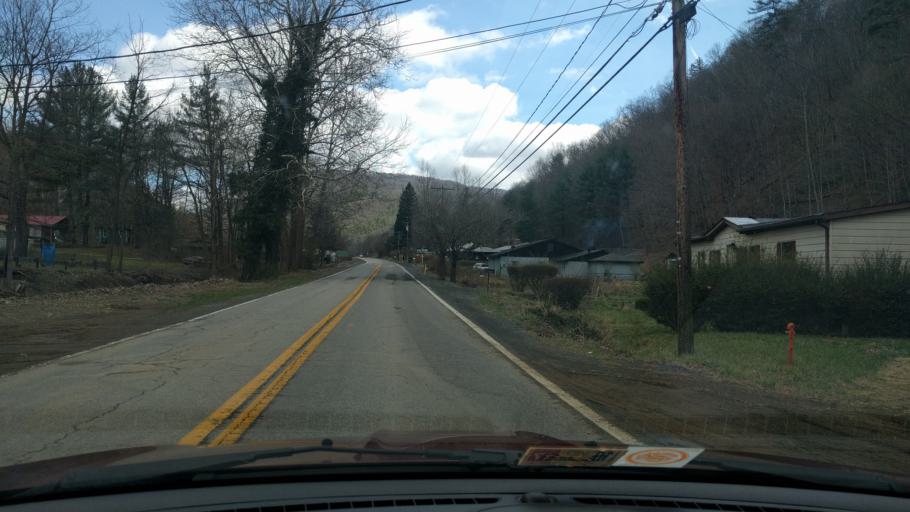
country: US
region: West Virginia
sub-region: Greenbrier County
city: White Sulphur Springs
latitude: 37.7979
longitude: -80.2789
